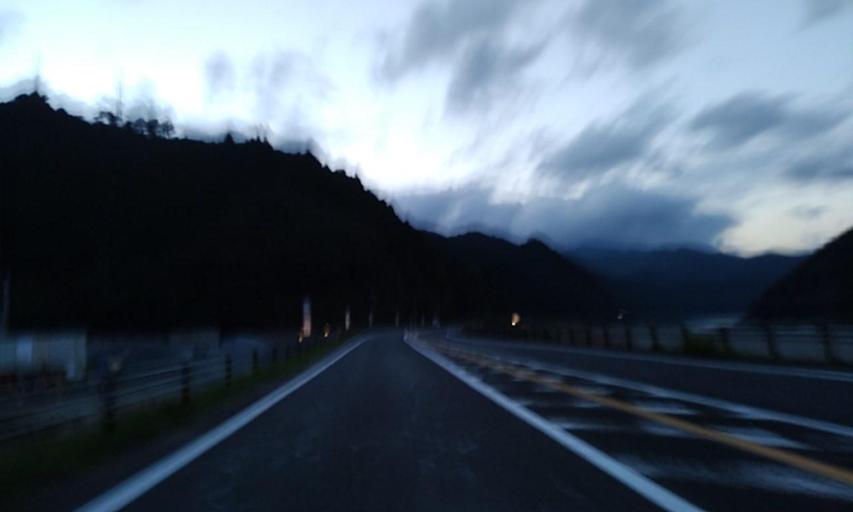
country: JP
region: Wakayama
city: Shingu
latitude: 33.7249
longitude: 135.9590
